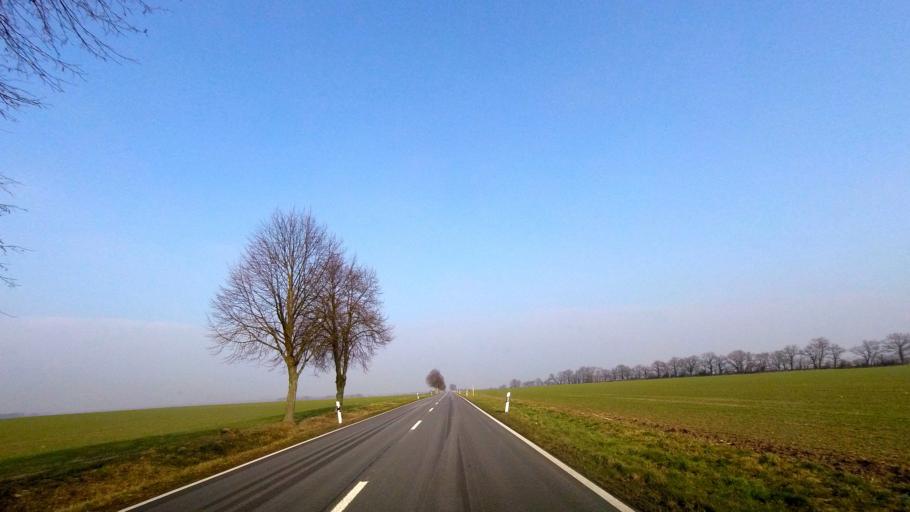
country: DE
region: Brandenburg
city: Niedergorsdorf
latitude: 51.9434
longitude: 13.0386
